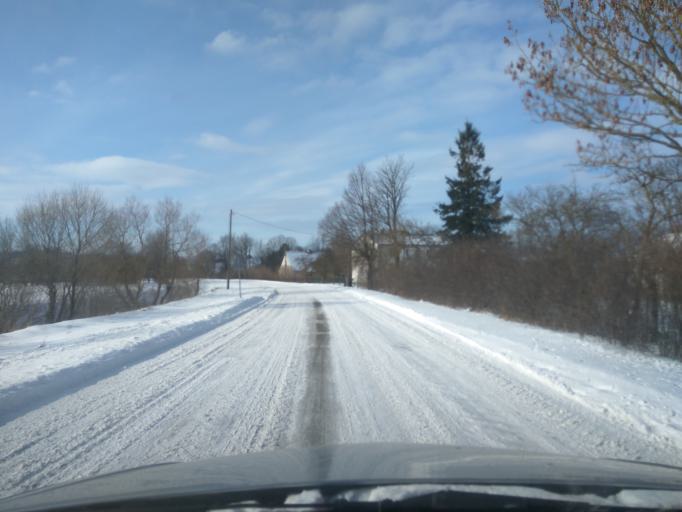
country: LV
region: Ventspils Rajons
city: Piltene
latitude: 57.3317
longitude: 21.6544
